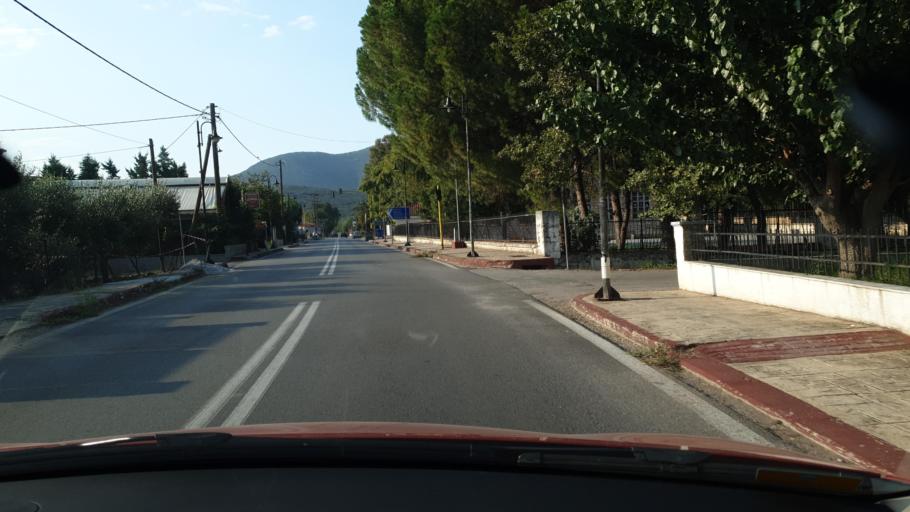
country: GR
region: Thessaly
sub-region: Nomos Magnisias
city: Sourpi
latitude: 39.1030
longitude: 22.8935
